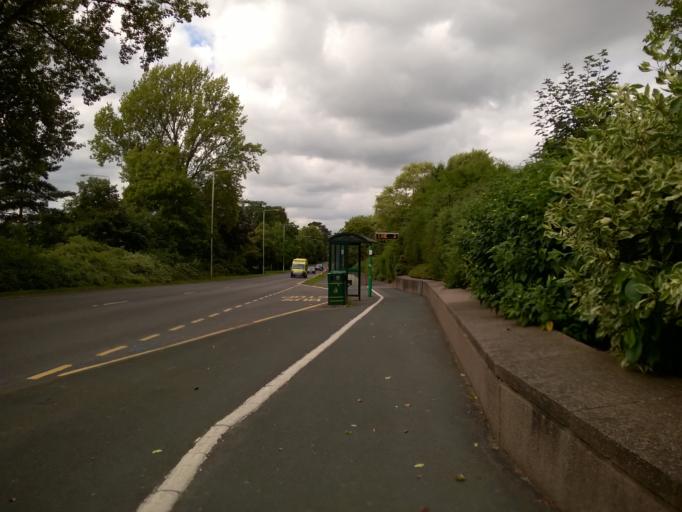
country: GB
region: England
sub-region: Leicestershire
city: Glenfield
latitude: 52.6552
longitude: -1.1893
